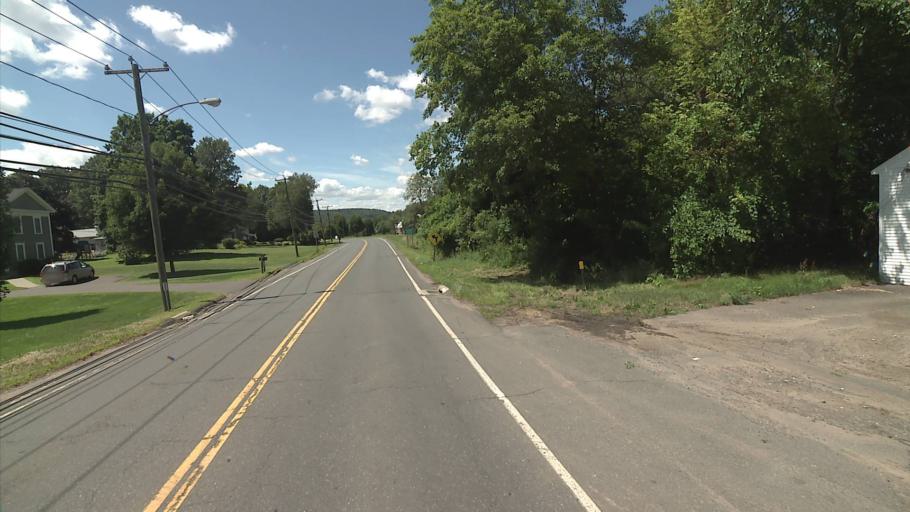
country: US
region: Connecticut
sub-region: Hartford County
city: Suffield Depot
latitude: 41.9920
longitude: -72.7030
